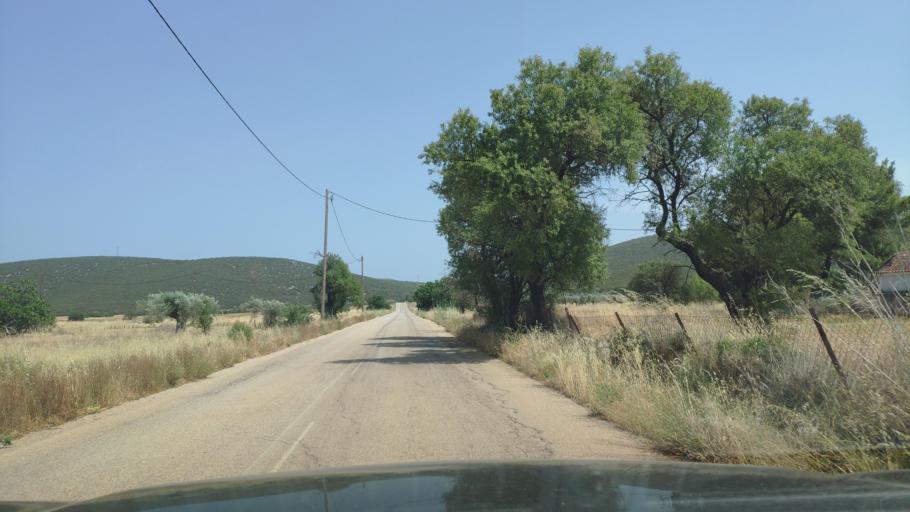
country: GR
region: Peloponnese
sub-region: Nomos Argolidos
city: Didyma
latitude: 37.4539
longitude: 23.1721
